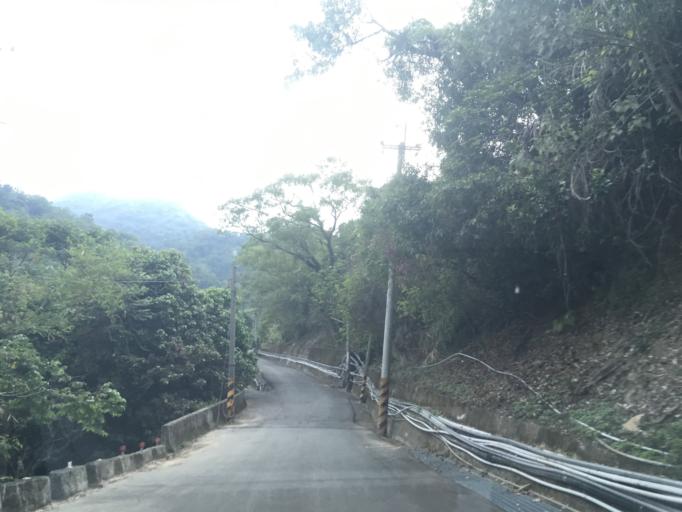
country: TW
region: Taiwan
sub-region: Nantou
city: Puli
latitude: 23.9542
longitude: 120.8623
